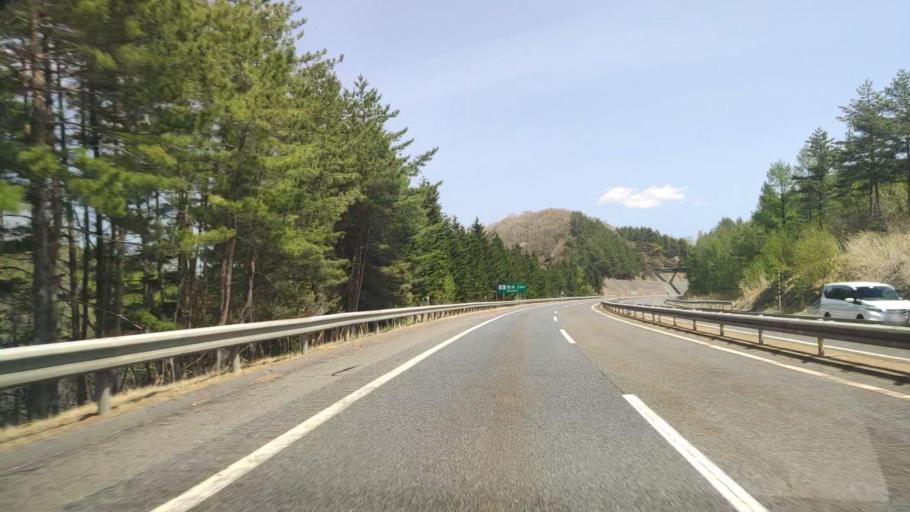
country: JP
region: Iwate
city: Ichinohe
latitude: 40.3118
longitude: 141.4321
